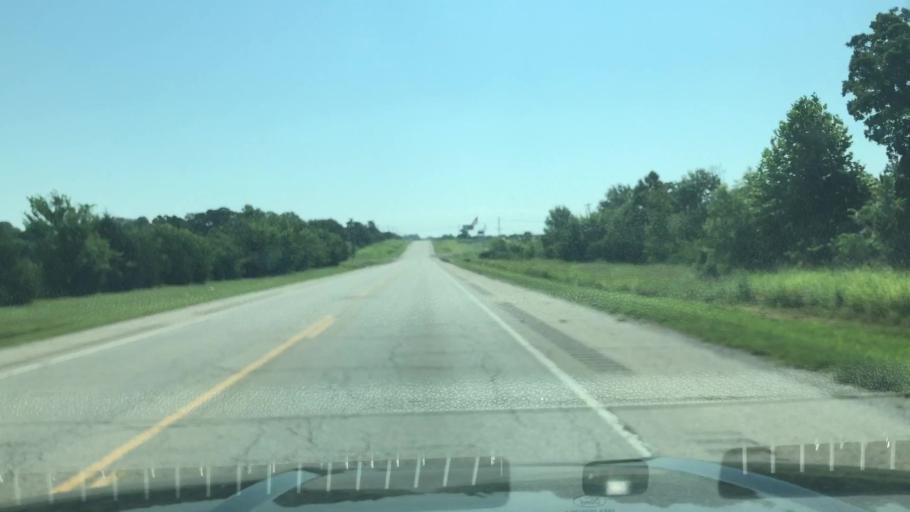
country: US
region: Oklahoma
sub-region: Creek County
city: Drumright
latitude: 35.9884
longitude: -96.5690
